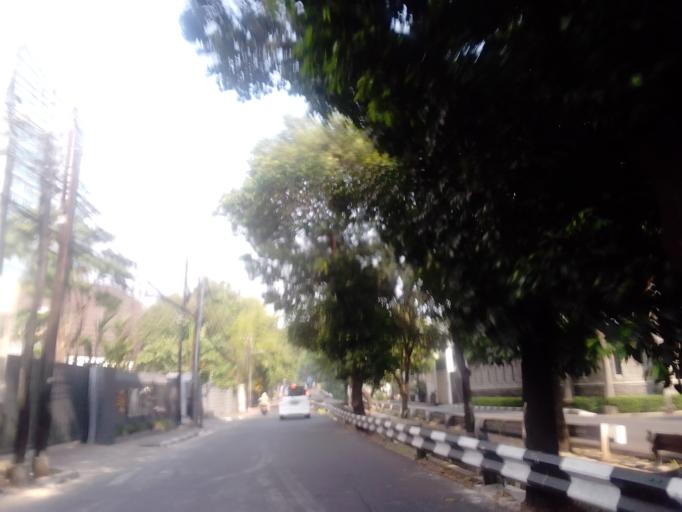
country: ID
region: Jakarta Raya
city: Jakarta
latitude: -6.2572
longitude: 106.8068
